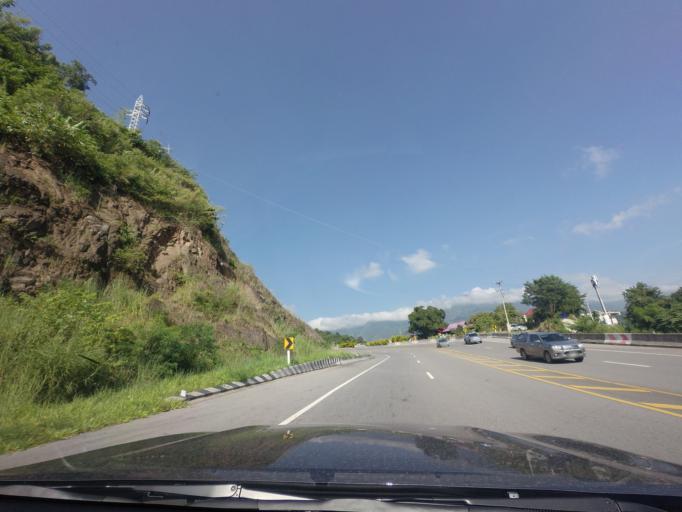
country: TH
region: Phetchabun
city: Khao Kho
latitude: 16.7824
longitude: 101.0970
